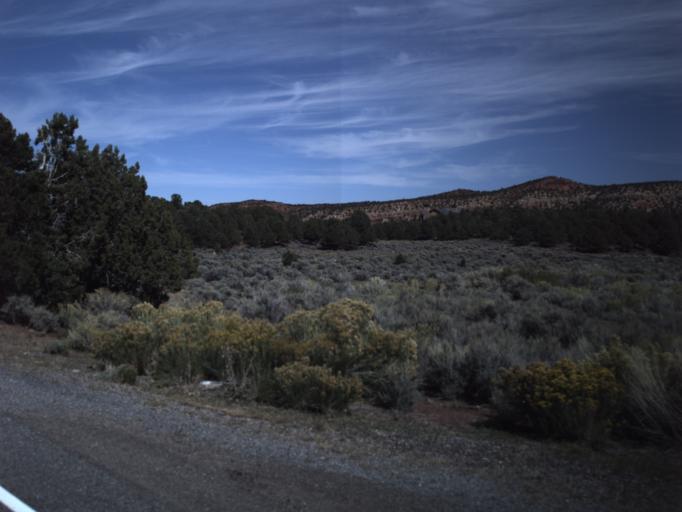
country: US
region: Utah
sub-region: Wayne County
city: Loa
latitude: 38.2100
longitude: -111.3477
